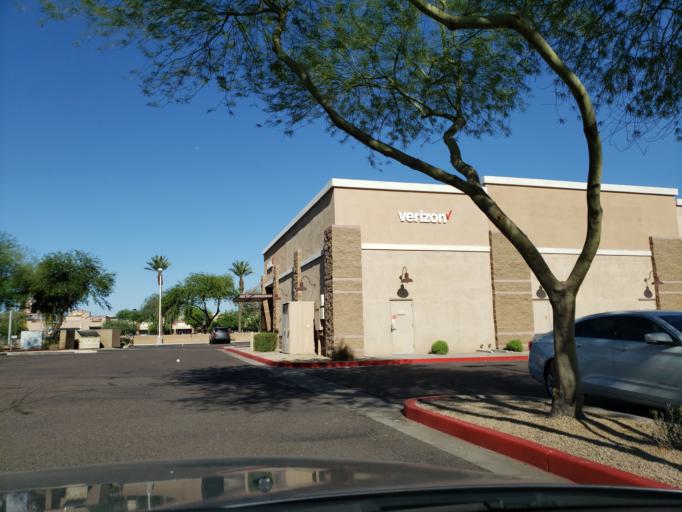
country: US
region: Arizona
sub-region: Maricopa County
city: Tolleson
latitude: 33.4634
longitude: -112.2715
